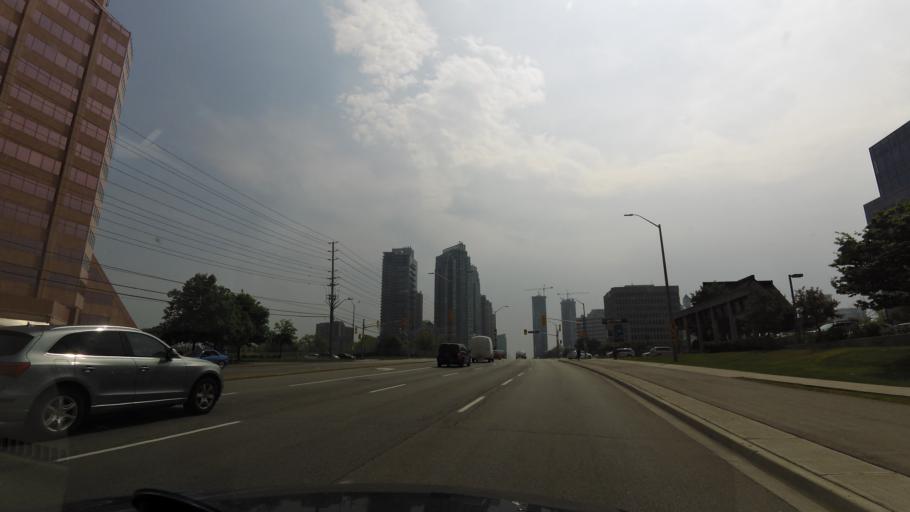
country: CA
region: Ontario
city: Mississauga
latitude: 43.5920
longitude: -79.6373
